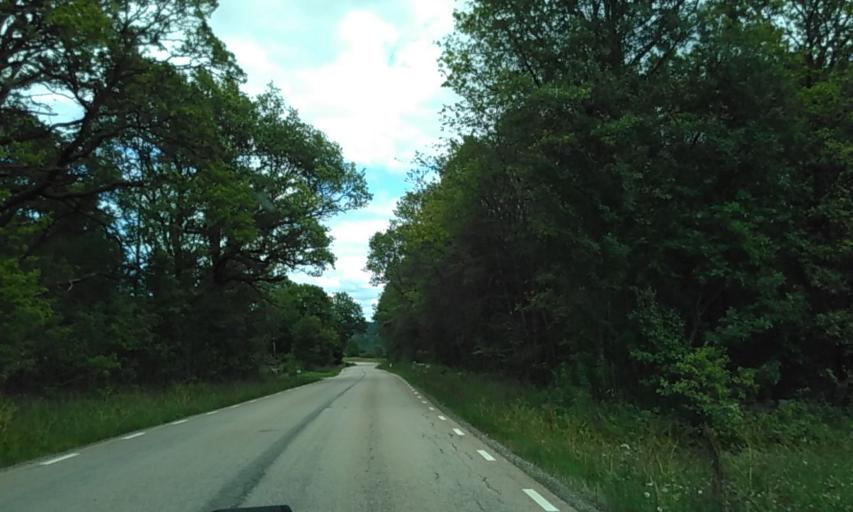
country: SE
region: Vaestra Goetaland
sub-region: Boras Kommun
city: Boras
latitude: 57.8017
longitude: 12.8931
